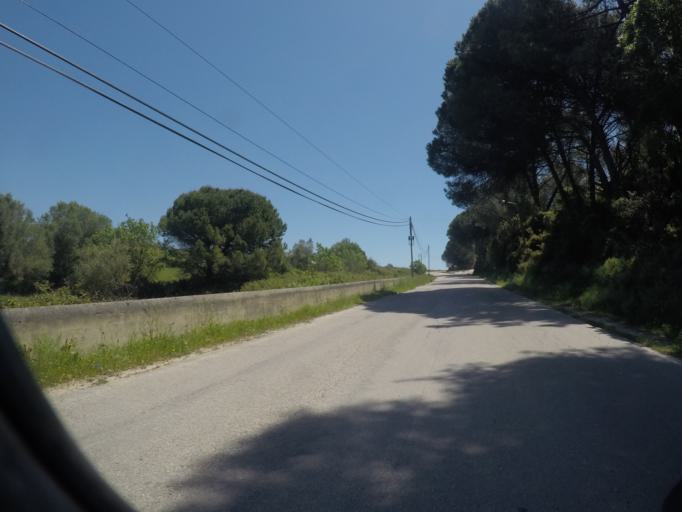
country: PT
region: Setubal
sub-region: Sesimbra
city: Sesimbra
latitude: 38.4646
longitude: -9.0808
